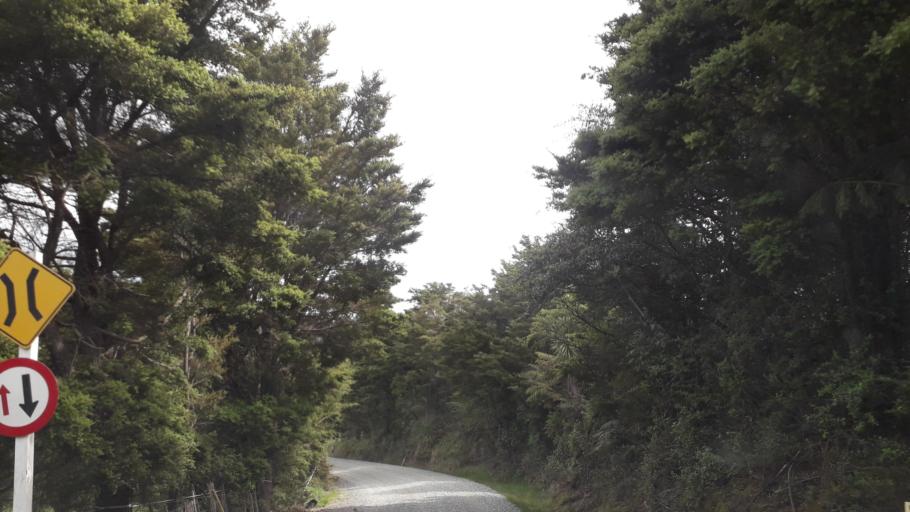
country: NZ
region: Northland
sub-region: Far North District
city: Kerikeri
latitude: -35.1307
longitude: 173.7395
